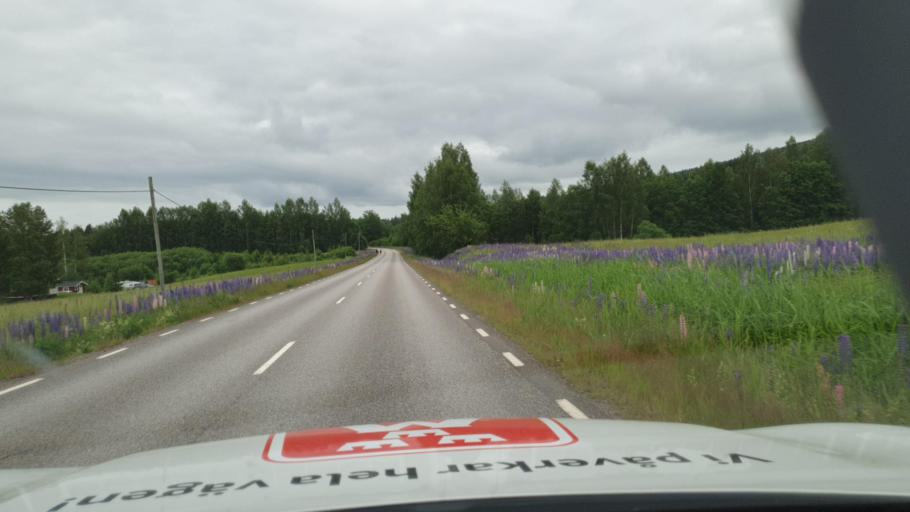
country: SE
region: Vaermland
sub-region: Sunne Kommun
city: Sunne
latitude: 59.8101
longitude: 13.0303
